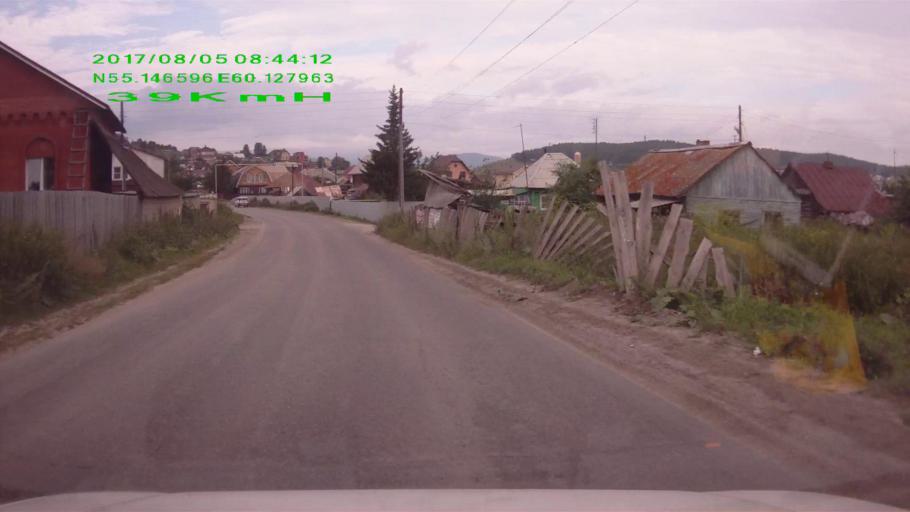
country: RU
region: Chelyabinsk
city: Turgoyak
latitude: 55.1466
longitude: 60.1273
